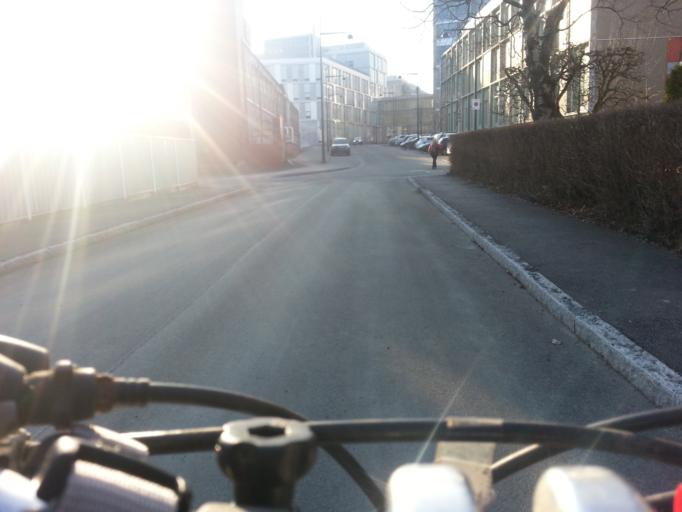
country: NO
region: Sor-Trondelag
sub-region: Trondheim
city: Trondheim
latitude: 63.4220
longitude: 10.3852
